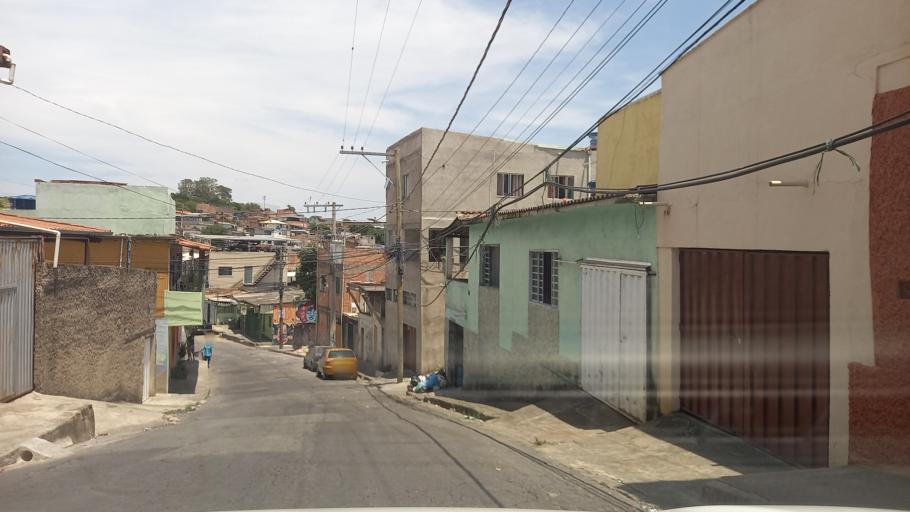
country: BR
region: Minas Gerais
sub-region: Contagem
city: Contagem
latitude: -19.9109
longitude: -44.0073
